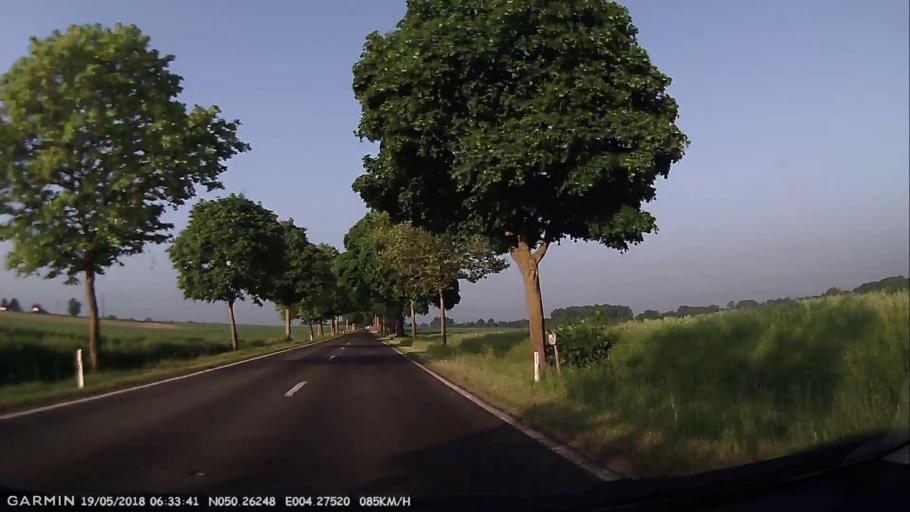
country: BE
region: Wallonia
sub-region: Province du Hainaut
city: Beaumont
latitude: 50.2624
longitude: 4.2751
